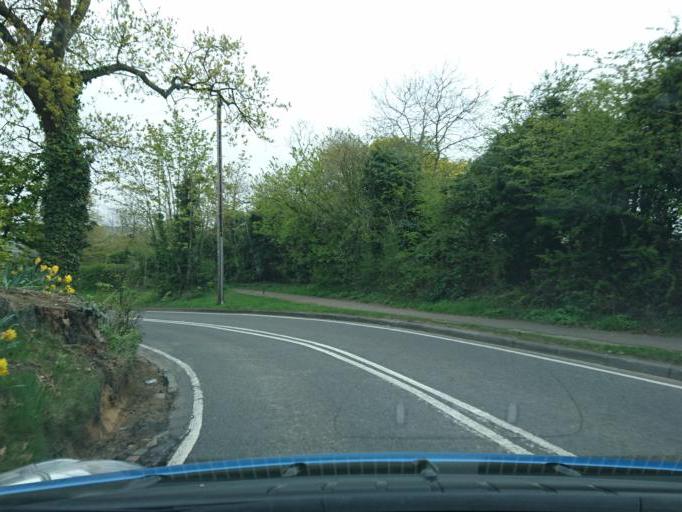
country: GB
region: England
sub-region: Greater London
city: Barnet
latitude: 51.6372
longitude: -0.1979
